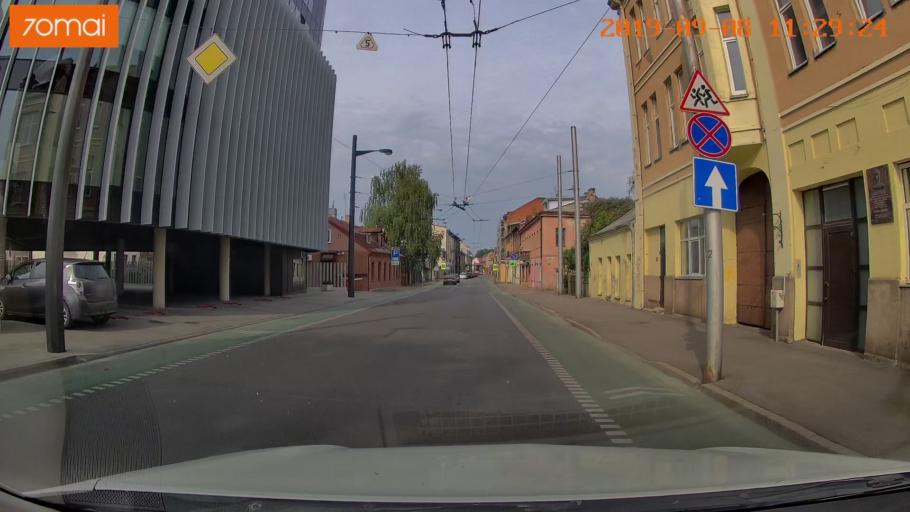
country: LT
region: Kauno apskritis
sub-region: Kaunas
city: Kaunas
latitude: 54.8947
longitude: 23.9020
